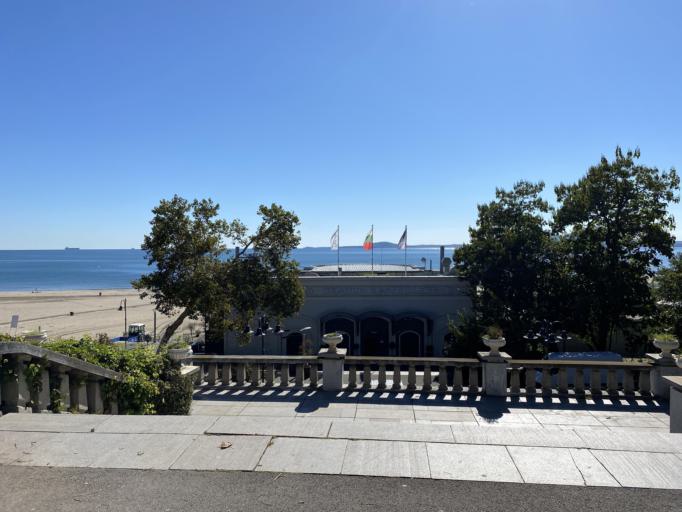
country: BG
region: Burgas
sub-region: Obshtina Burgas
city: Burgas
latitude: 42.4924
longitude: 27.4807
